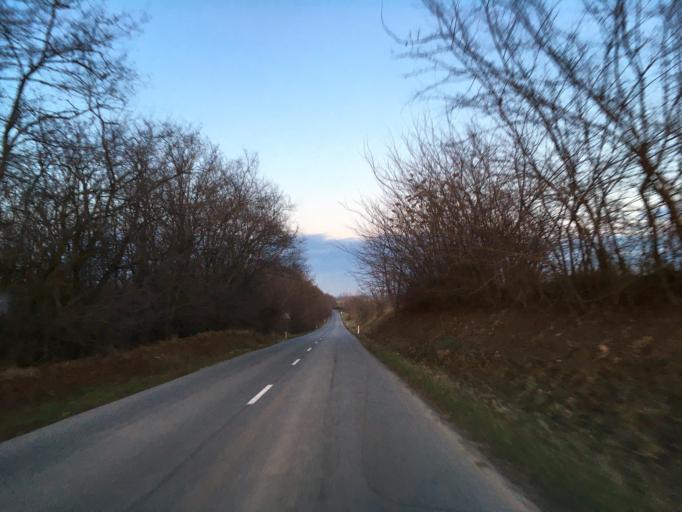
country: SK
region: Nitriansky
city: Svodin
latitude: 47.8598
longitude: 18.4540
